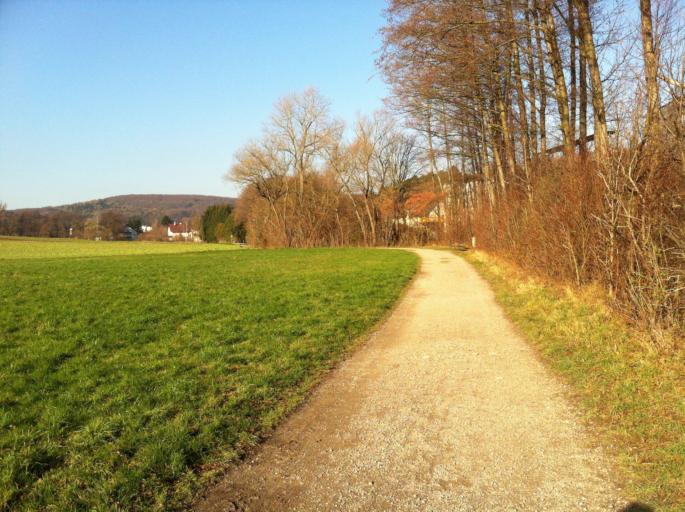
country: AT
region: Lower Austria
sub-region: Politischer Bezirk Wien-Umgebung
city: Gablitz
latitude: 48.2322
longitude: 16.1445
